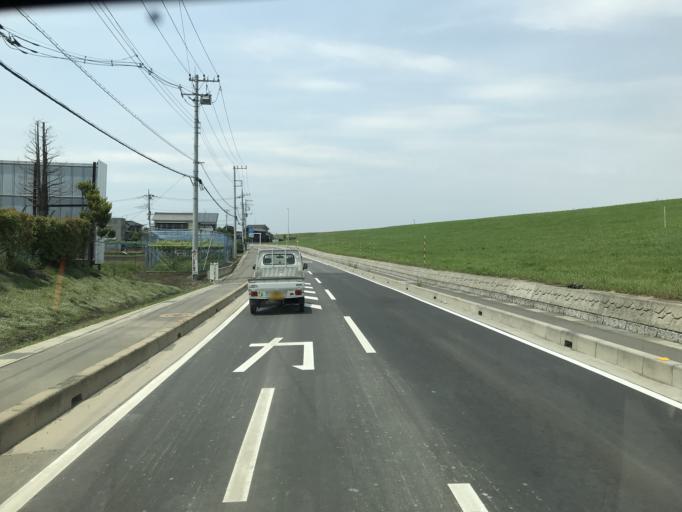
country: JP
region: Ibaraki
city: Sakai
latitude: 36.0348
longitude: 139.8127
